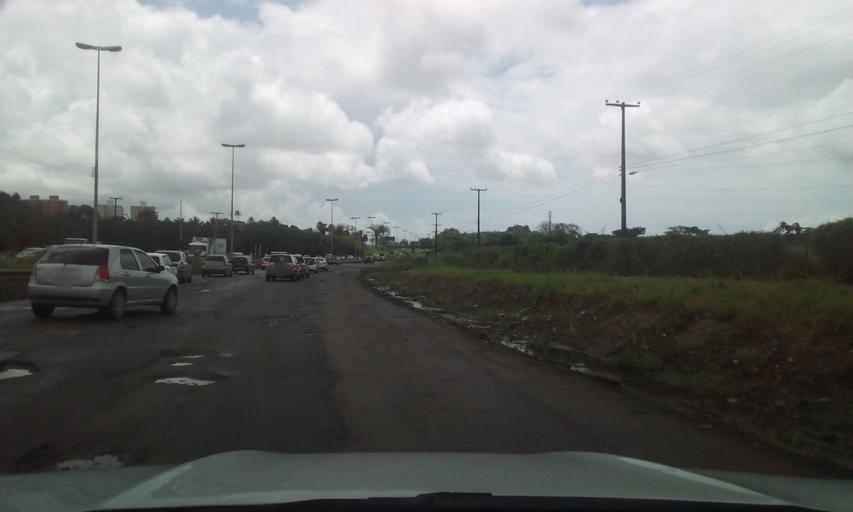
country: BR
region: Pernambuco
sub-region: Jaboatao Dos Guararapes
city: Jaboatao dos Guararapes
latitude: -8.0973
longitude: -34.9499
